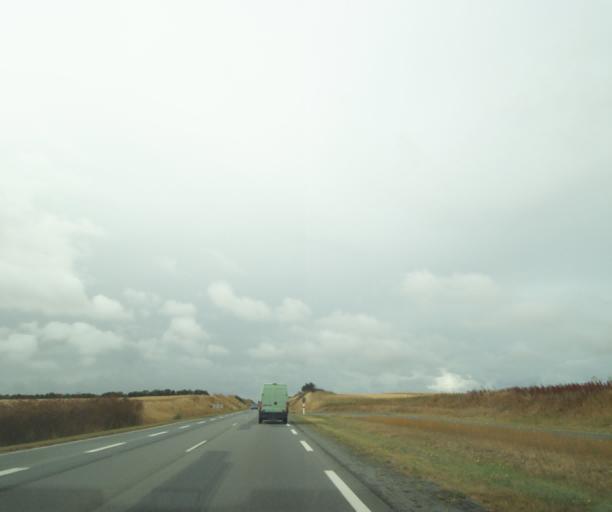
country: FR
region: Poitou-Charentes
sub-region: Departement de la Charente-Maritime
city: Lagord
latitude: 46.2028
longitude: -1.1383
